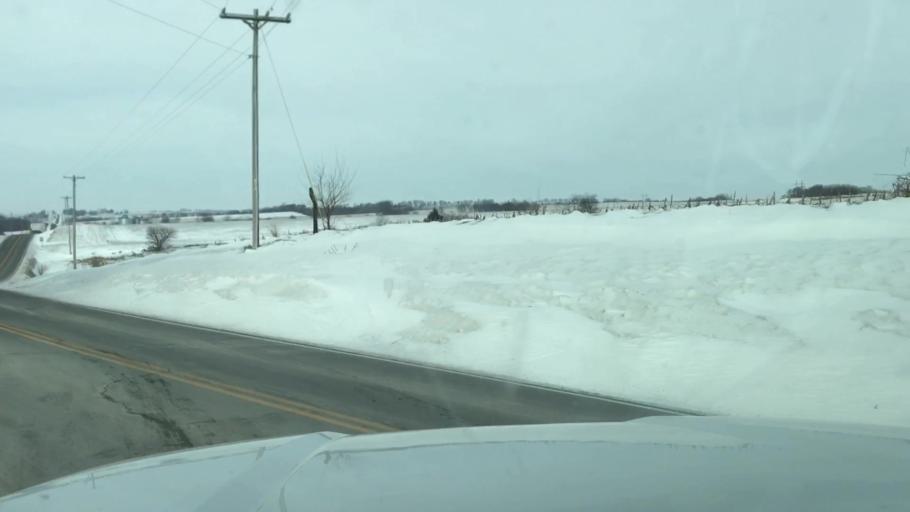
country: US
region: Missouri
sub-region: Holt County
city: Mound City
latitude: 40.1302
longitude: -95.0909
